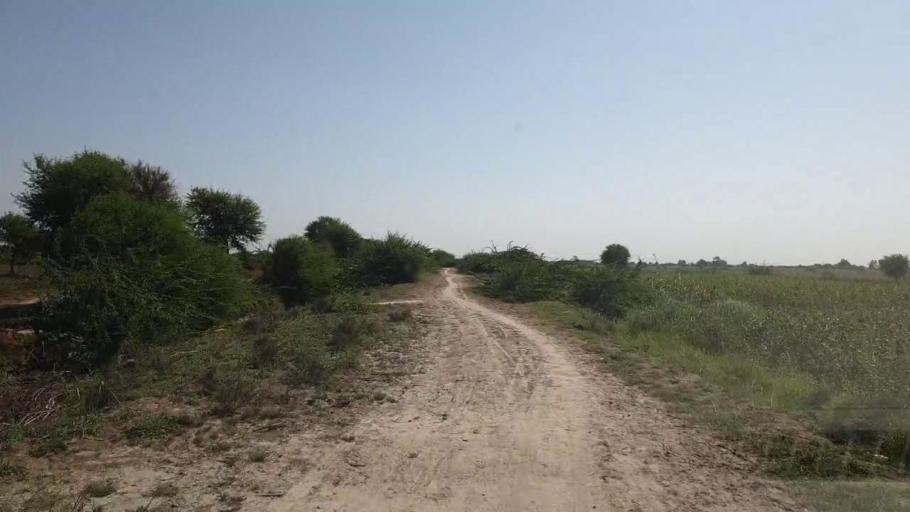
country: PK
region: Sindh
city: Kadhan
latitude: 24.5962
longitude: 69.0056
